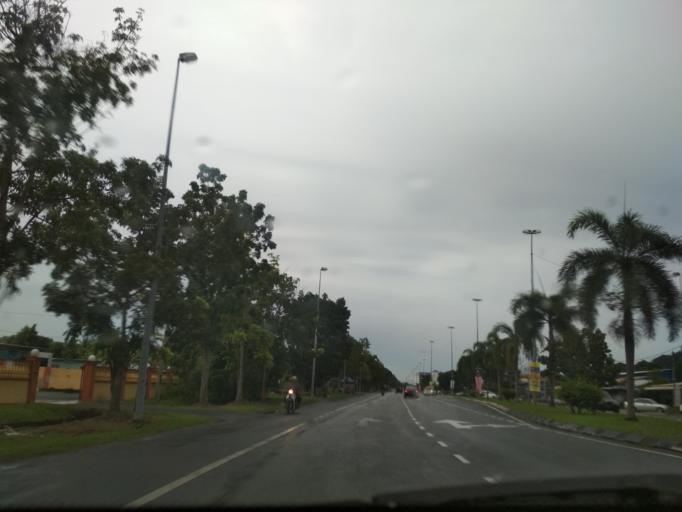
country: MY
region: Perlis
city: Kangar
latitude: 6.4211
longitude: 100.1838
